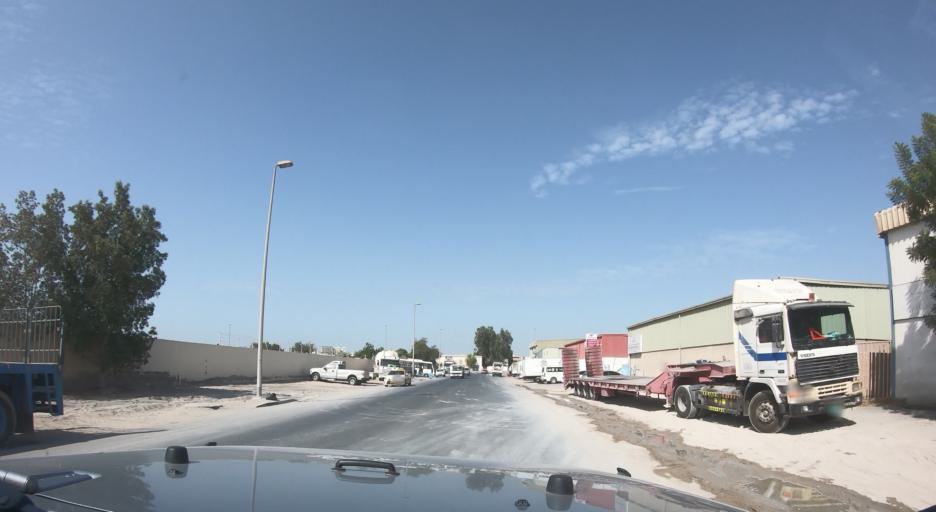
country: AE
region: Dubai
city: Dubai
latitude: 25.1492
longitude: 55.2312
